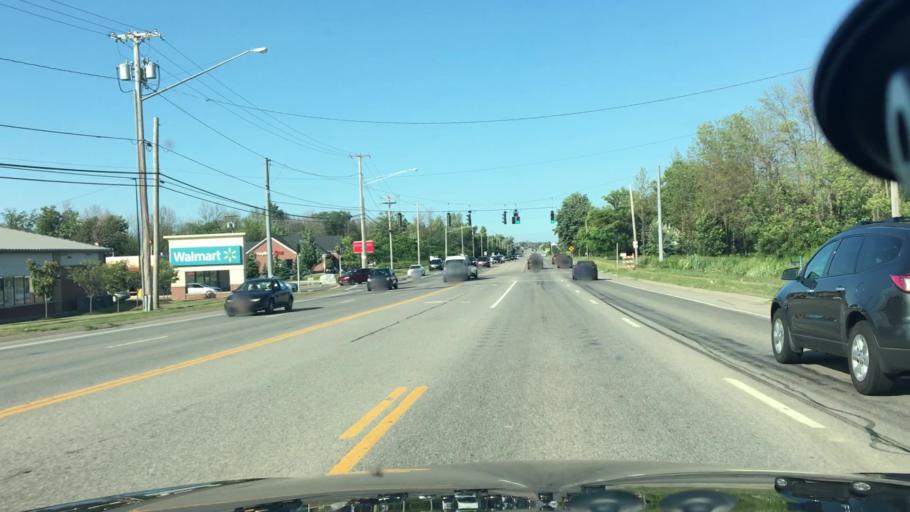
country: US
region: New York
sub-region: Erie County
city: Wanakah
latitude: 42.7412
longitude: -78.8701
